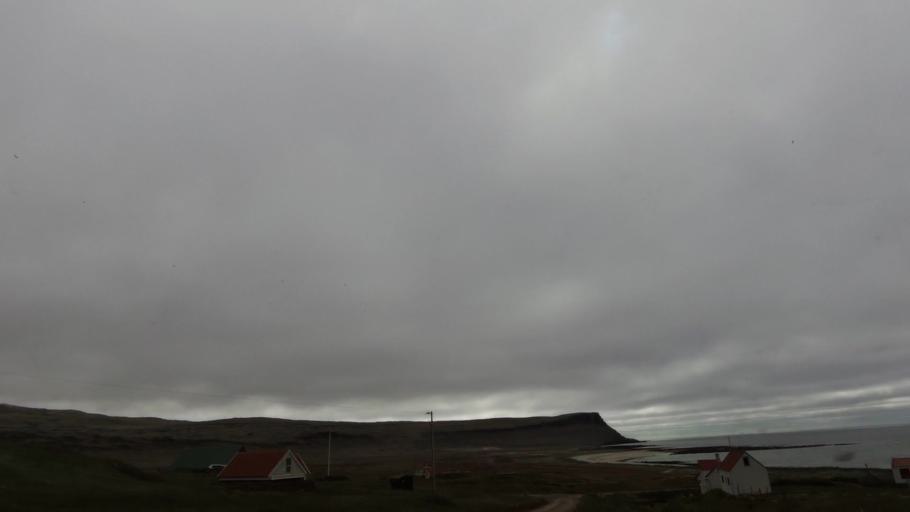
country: IS
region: West
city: Olafsvik
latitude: 65.5289
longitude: -24.4558
